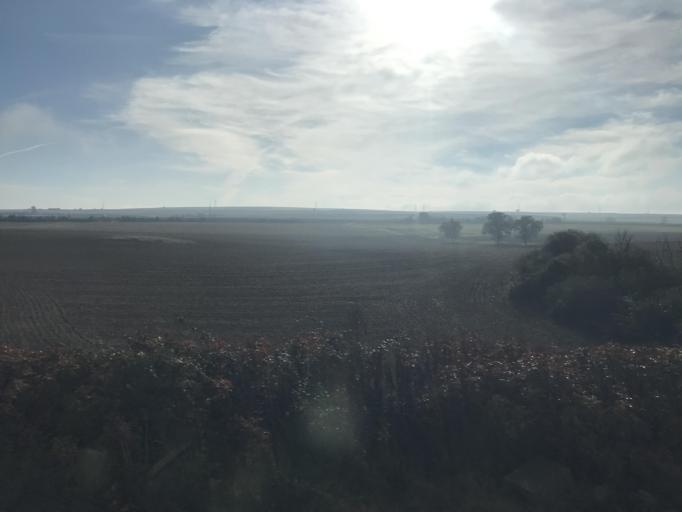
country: ES
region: Castille and Leon
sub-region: Provincia de Burgos
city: Aguilar de Bureba
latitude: 42.5887
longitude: -3.2977
